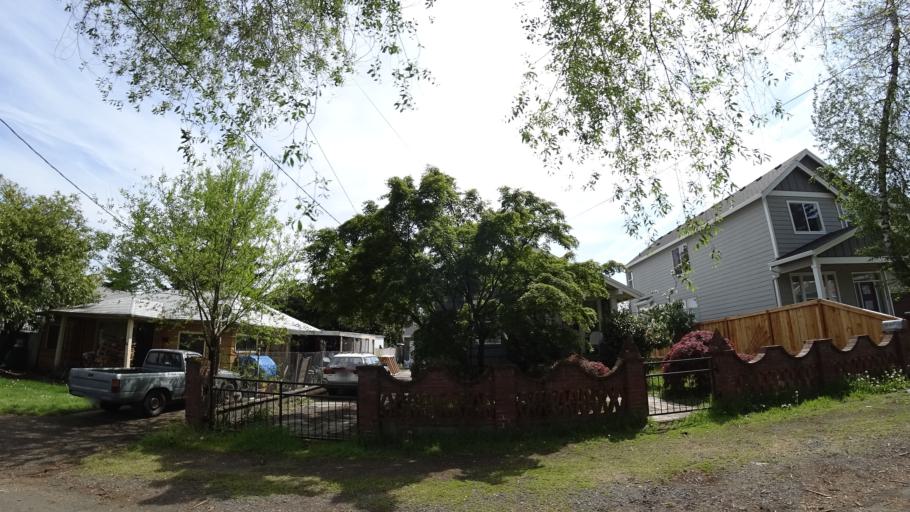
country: US
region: Oregon
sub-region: Clackamas County
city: Milwaukie
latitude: 45.4693
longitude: -122.6092
